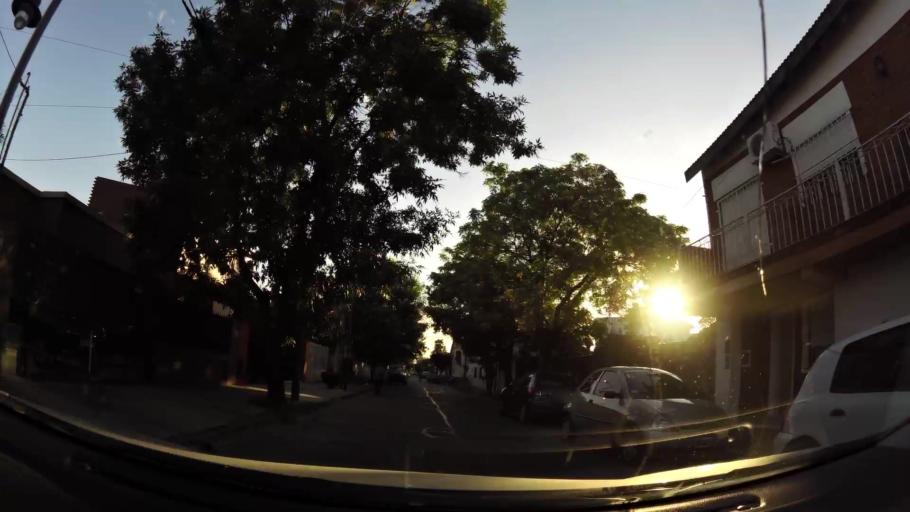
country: AR
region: Buenos Aires
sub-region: Partido de Tigre
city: Tigre
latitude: -34.4466
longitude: -58.5598
